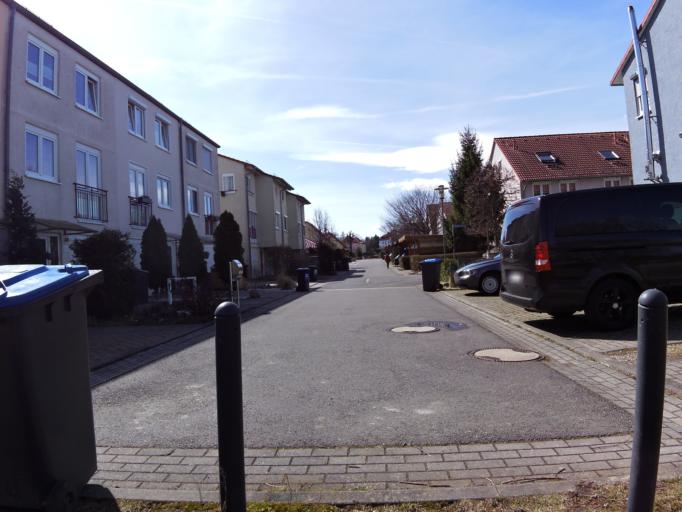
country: DE
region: Saxony
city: Borsdorf
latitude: 51.3388
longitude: 12.4952
